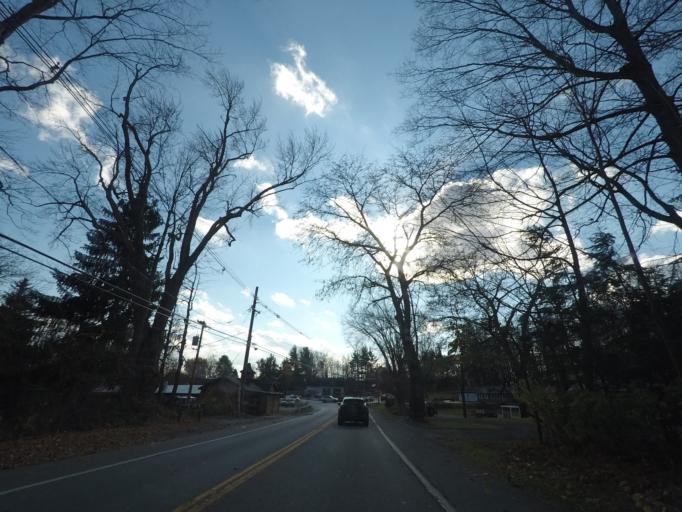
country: US
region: New York
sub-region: Schenectady County
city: East Glenville
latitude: 42.9052
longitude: -73.8967
